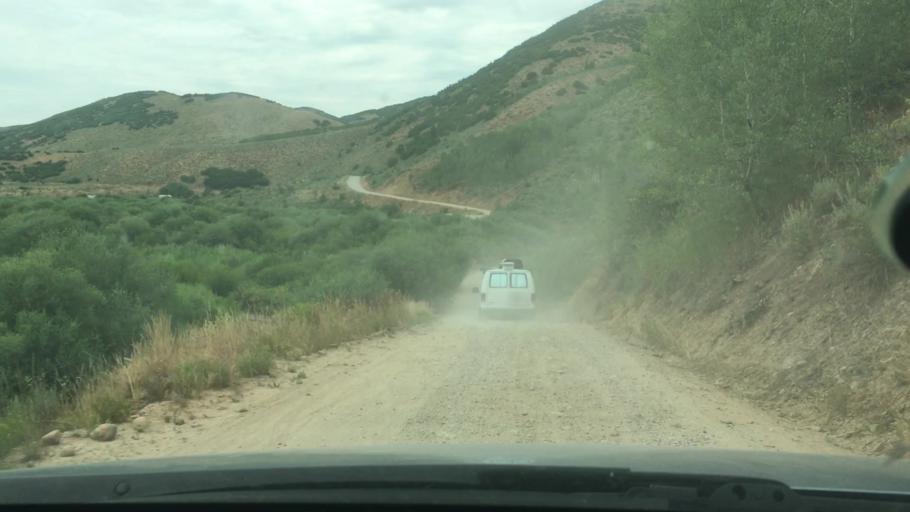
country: US
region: Utah
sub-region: Summit County
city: Summit Park
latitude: 40.8135
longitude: -111.5872
